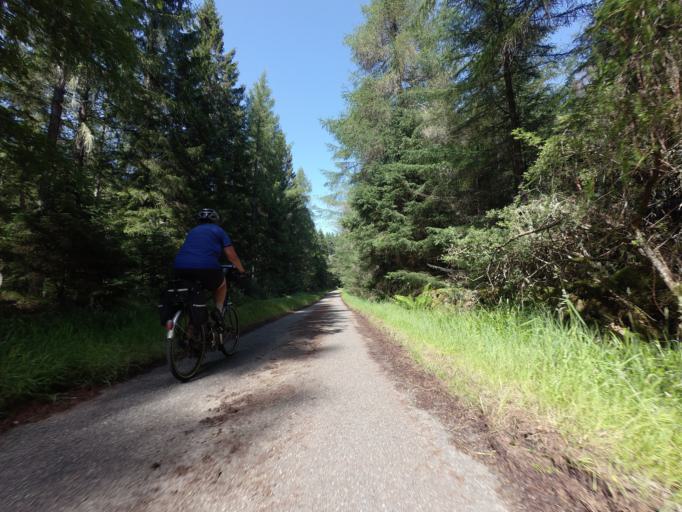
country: GB
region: Scotland
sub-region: Highland
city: Nairn
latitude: 57.5023
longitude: -3.9314
